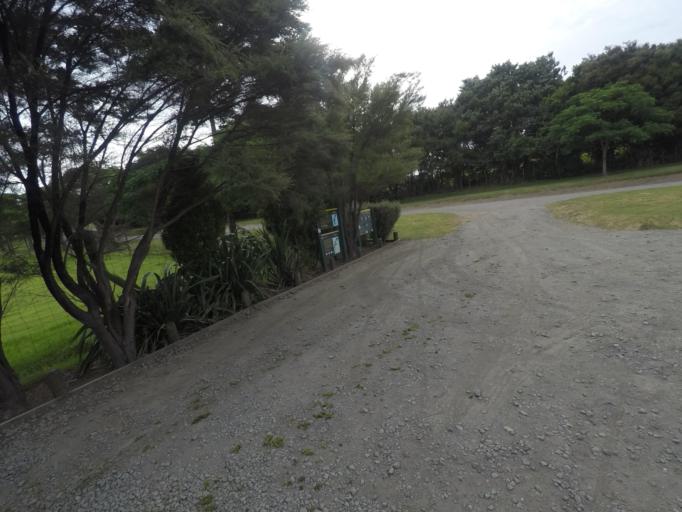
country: NZ
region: Auckland
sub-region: Auckland
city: Parakai
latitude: -36.5160
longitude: 174.2441
